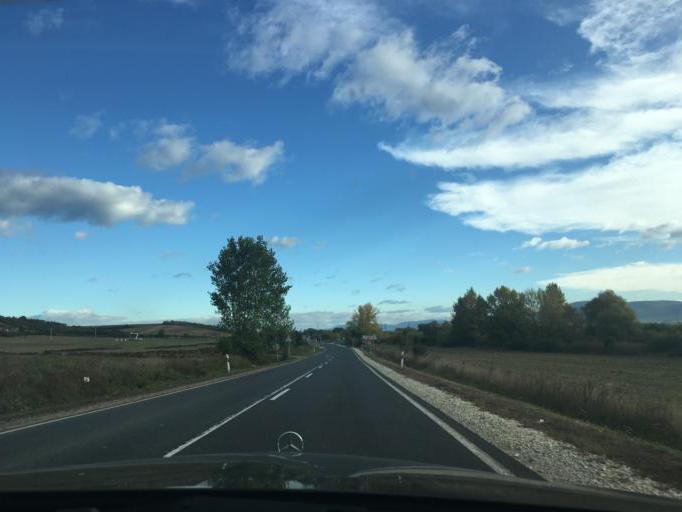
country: HU
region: Borsod-Abauj-Zemplen
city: Encs
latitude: 48.3863
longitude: 21.1536
